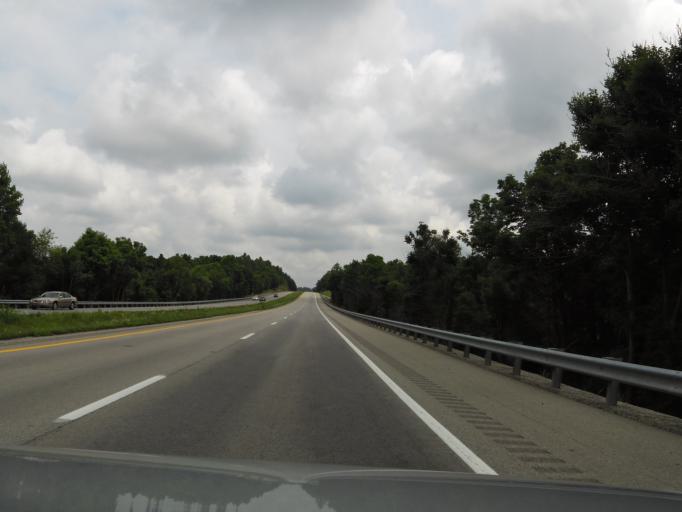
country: US
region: Kentucky
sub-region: Grayson County
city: Leitchfield
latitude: 37.5052
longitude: -86.1594
